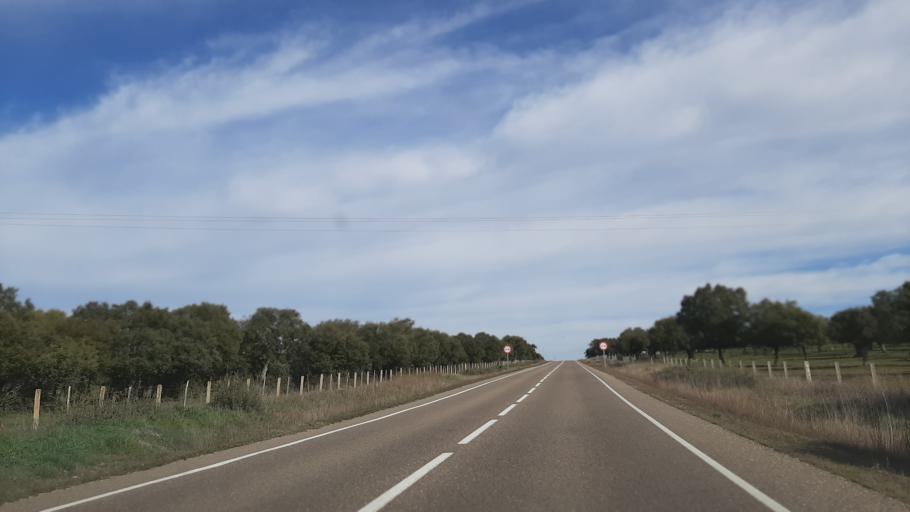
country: ES
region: Castille and Leon
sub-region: Provincia de Salamanca
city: Ledesma
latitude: 41.0898
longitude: -5.9549
